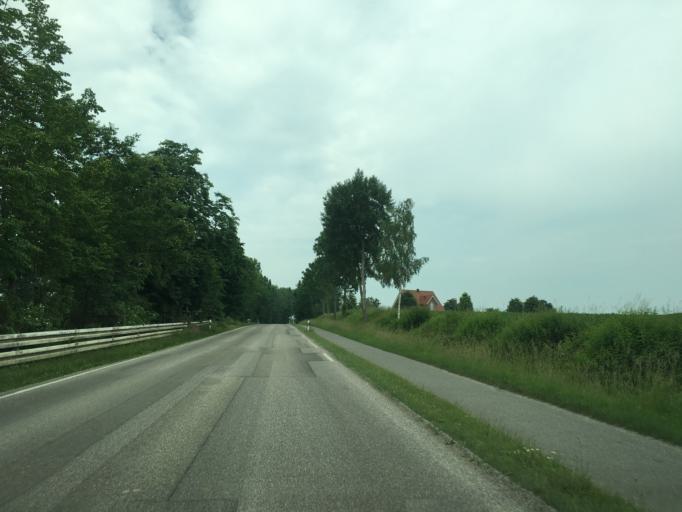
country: DE
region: North Rhine-Westphalia
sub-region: Regierungsbezirk Munster
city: Nordwalde
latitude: 52.0642
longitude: 7.4831
